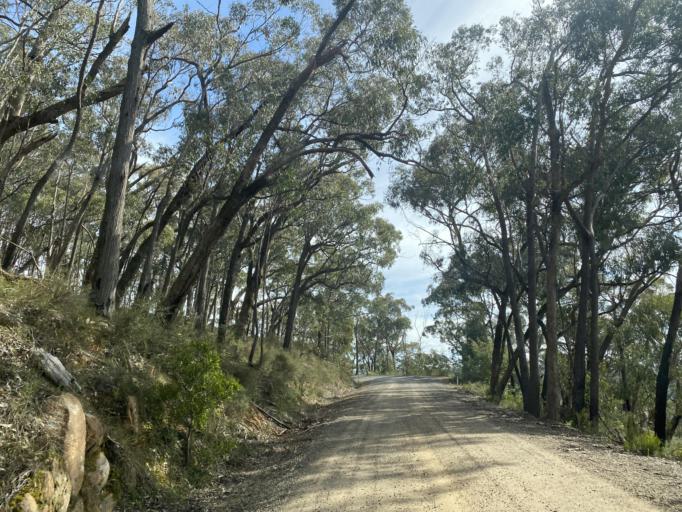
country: AU
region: Victoria
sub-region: Mansfield
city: Mansfield
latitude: -36.8434
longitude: 146.1666
